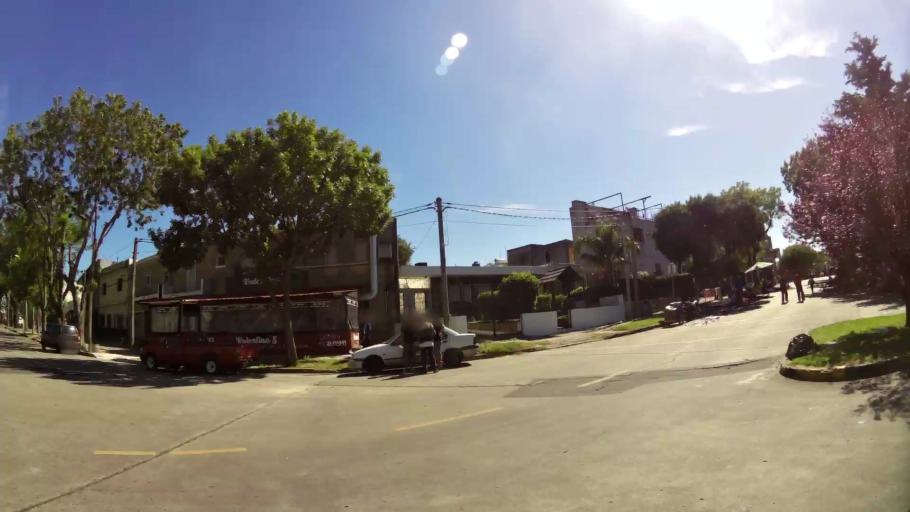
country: UY
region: Montevideo
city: Montevideo
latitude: -34.8889
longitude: -56.1238
